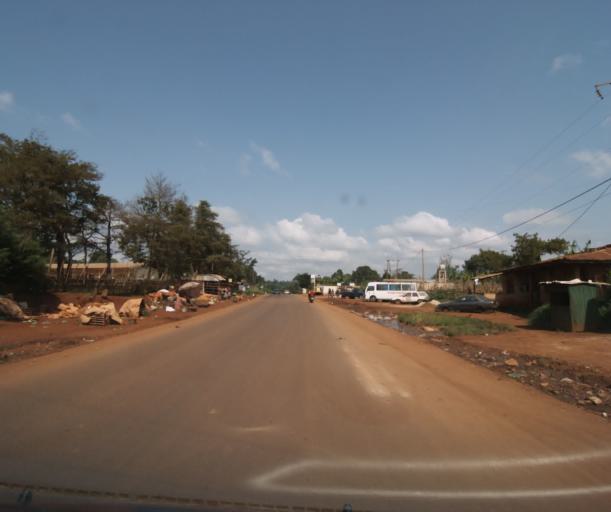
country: CM
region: West
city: Bansoa
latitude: 5.5011
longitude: 10.2407
